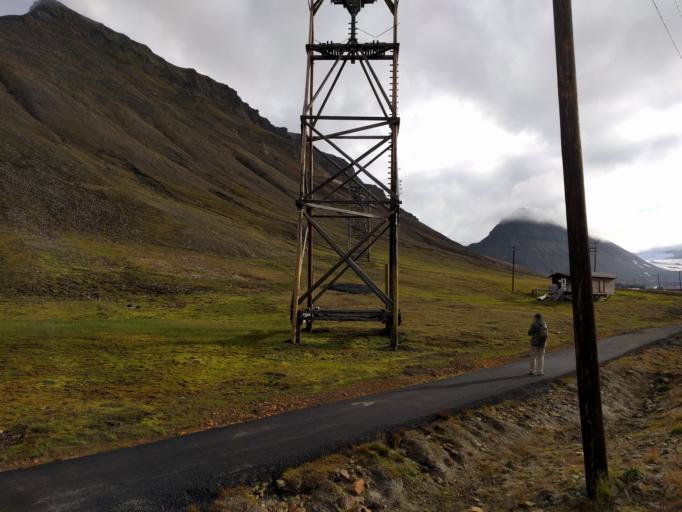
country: SJ
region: Svalbard
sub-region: Spitsbergen
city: Longyearbyen
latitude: 78.2101
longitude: 15.6158
